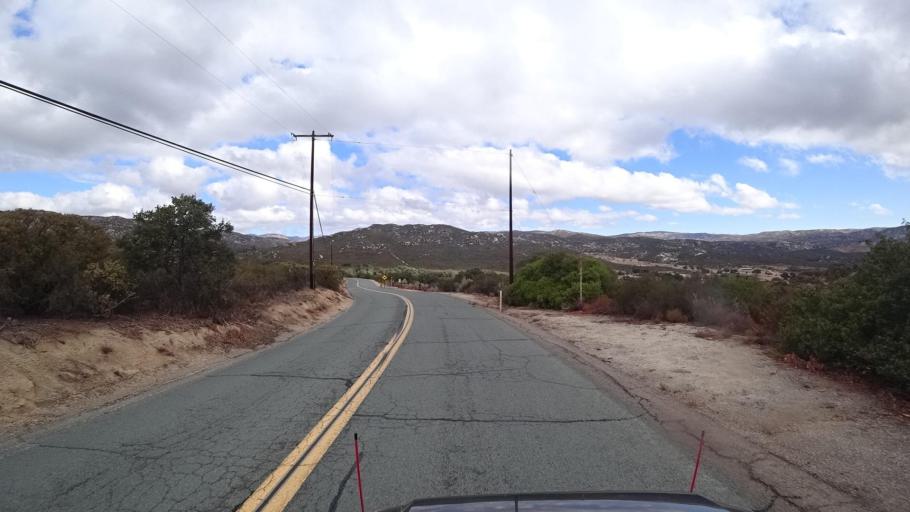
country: US
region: California
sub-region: San Diego County
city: Campo
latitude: 32.6771
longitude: -116.4290
